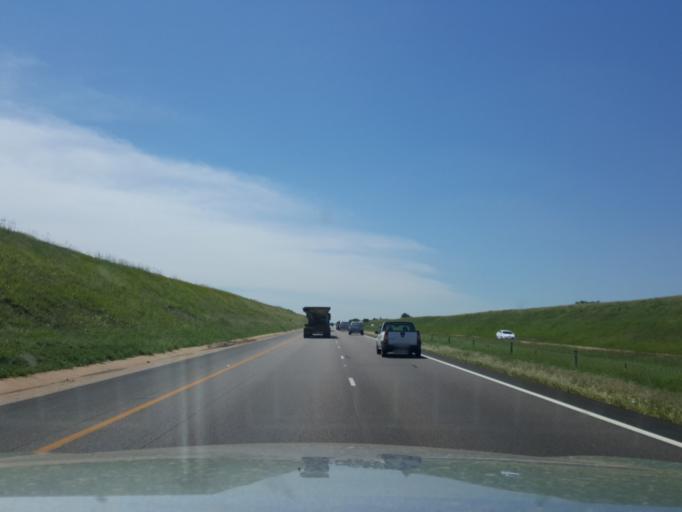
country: ZA
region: Gauteng
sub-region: City of Tshwane Metropolitan Municipality
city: Pretoria
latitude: -25.6392
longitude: 28.2117
